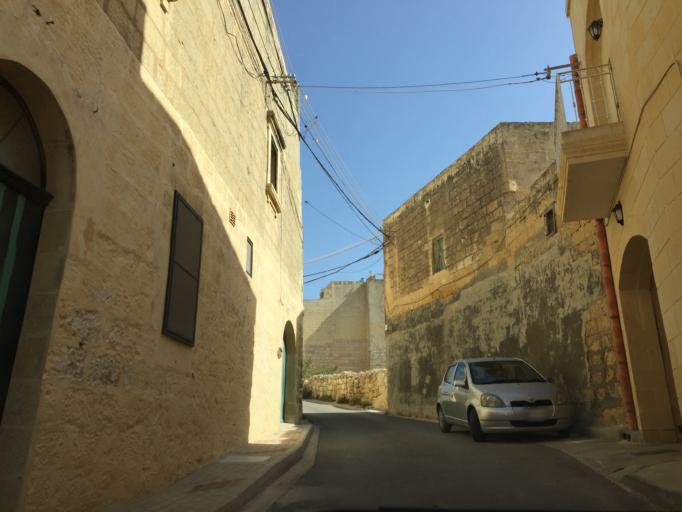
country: MT
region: L-Gharb
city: Gharb
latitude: 36.0642
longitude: 14.2066
